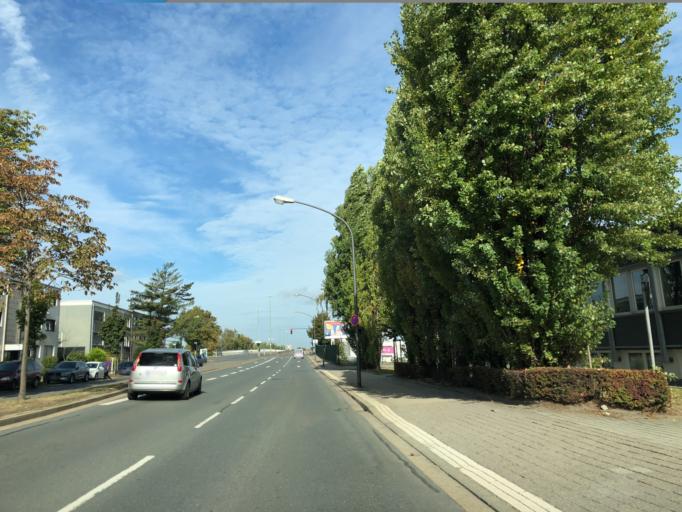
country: DE
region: North Rhine-Westphalia
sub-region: Regierungsbezirk Dusseldorf
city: Essen
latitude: 51.4622
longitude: 7.0295
